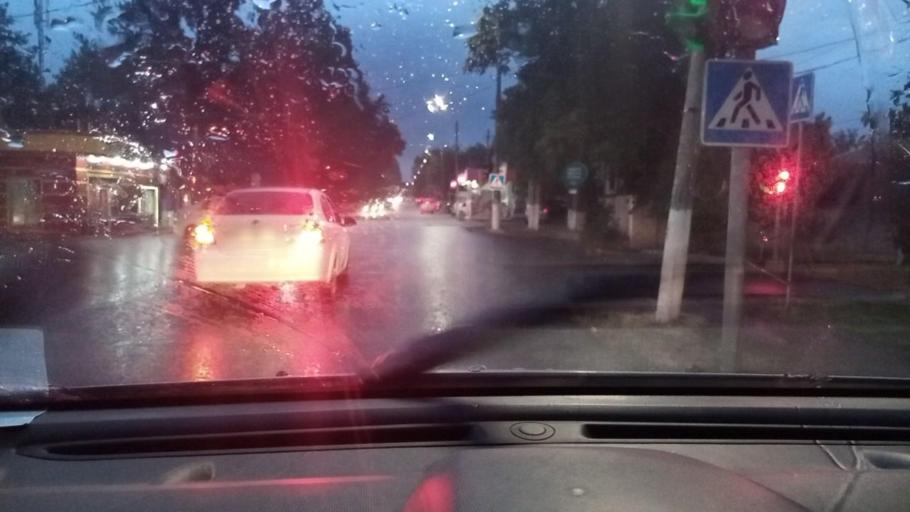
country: UZ
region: Toshkent
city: Salor
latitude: 41.3205
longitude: 69.3430
